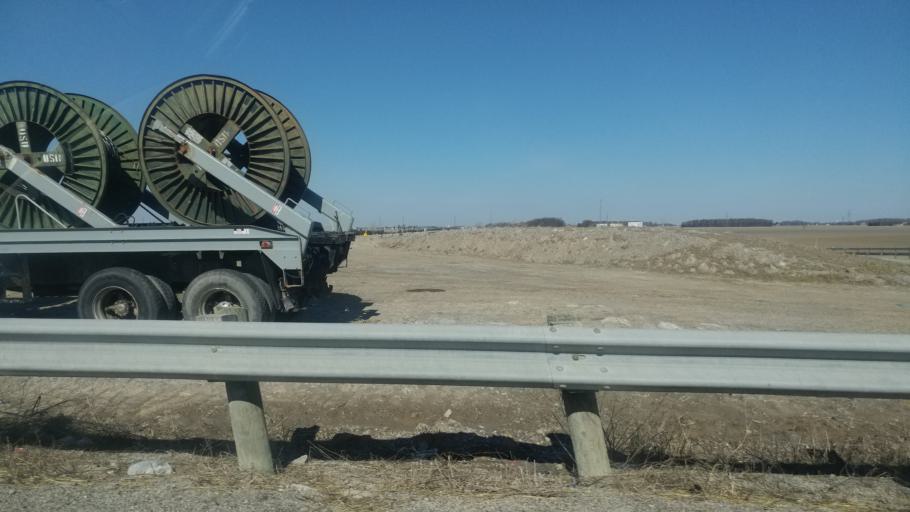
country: US
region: Ohio
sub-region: Wood County
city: Haskins
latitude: 41.4580
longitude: -83.6211
